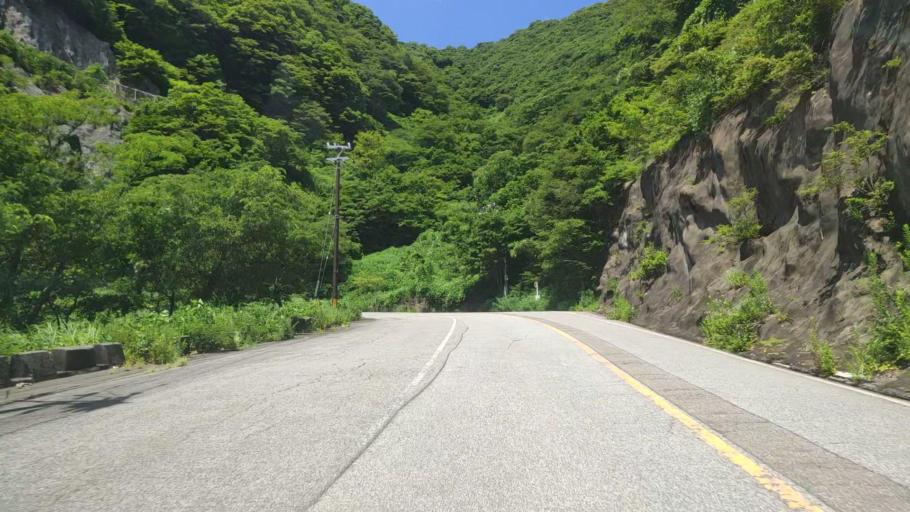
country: JP
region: Fukui
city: Ono
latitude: 35.9221
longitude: 136.5428
